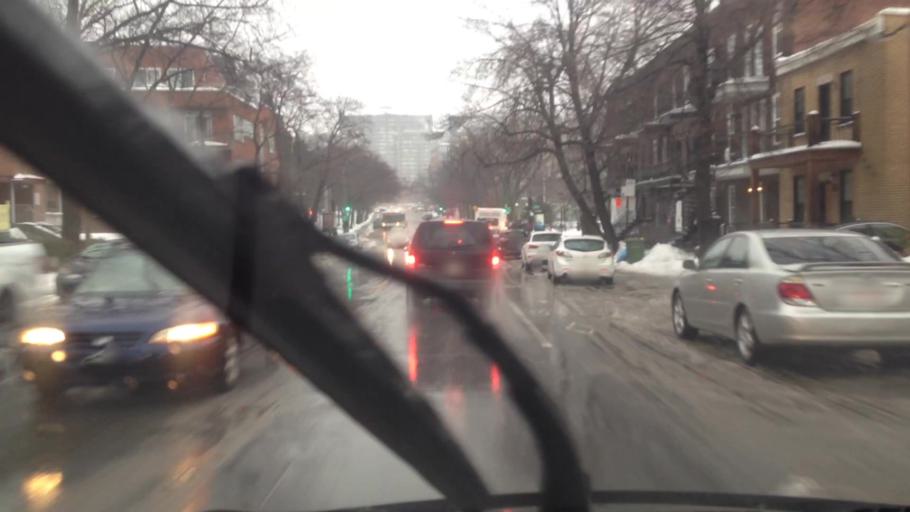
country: CA
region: Quebec
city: Westmount
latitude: 45.4984
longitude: -73.6209
